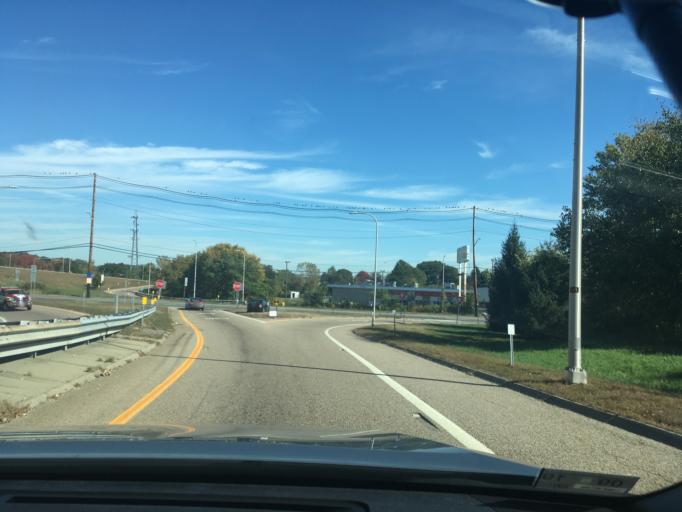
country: US
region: Rhode Island
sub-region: Providence County
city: North Providence
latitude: 41.8208
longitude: -71.4706
